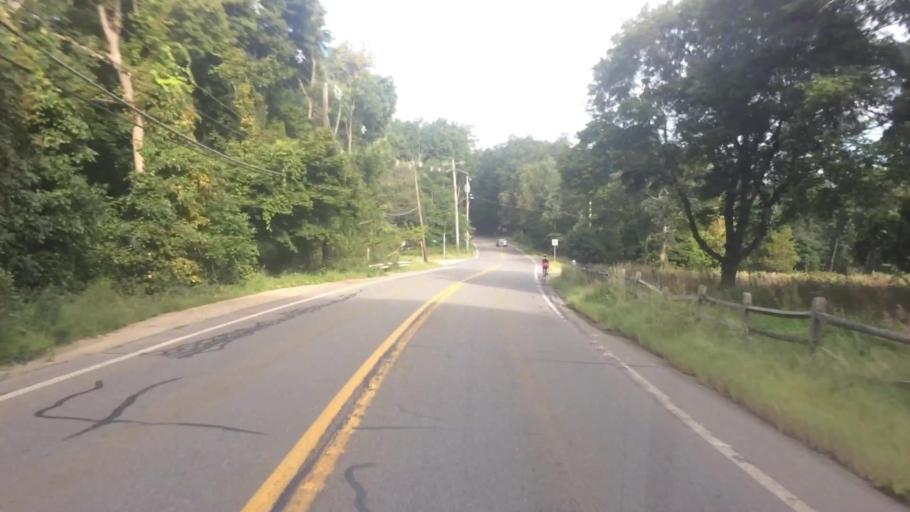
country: US
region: Massachusetts
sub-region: Middlesex County
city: Lincoln
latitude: 42.4494
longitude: -71.2883
